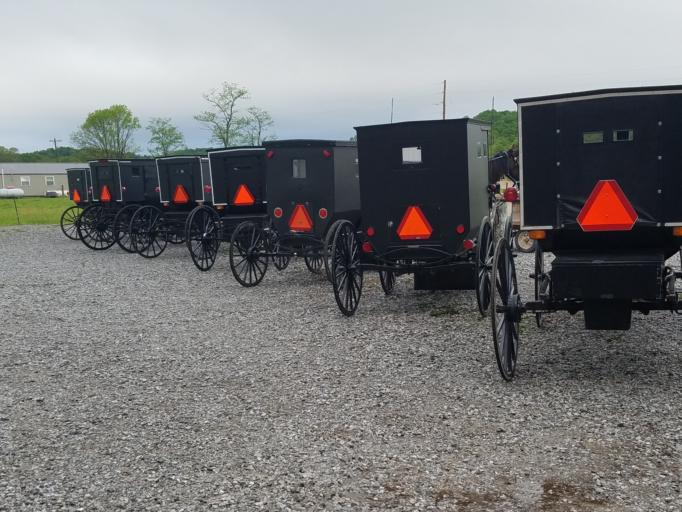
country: US
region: Kentucky
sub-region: Taylor County
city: Campbellsville
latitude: 37.3961
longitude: -85.1825
